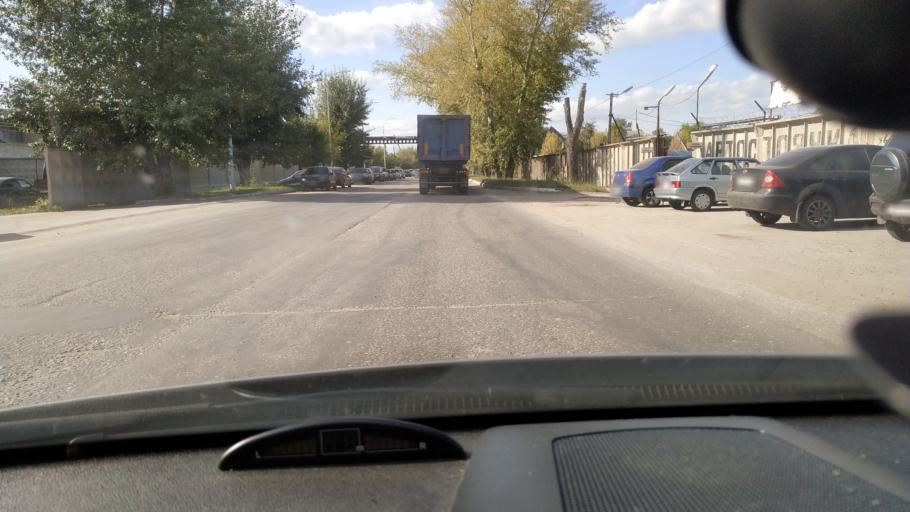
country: RU
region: Rjazan
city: Ryazan'
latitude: 54.6562
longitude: 39.6376
